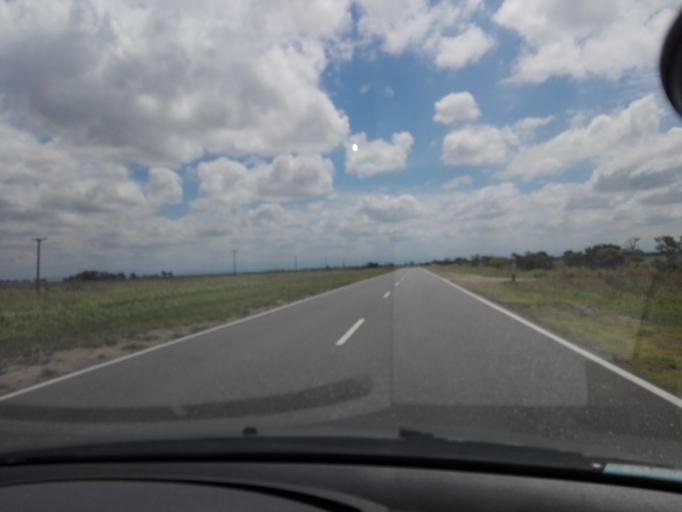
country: AR
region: Cordoba
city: Toledo
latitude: -31.6463
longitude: -64.0408
